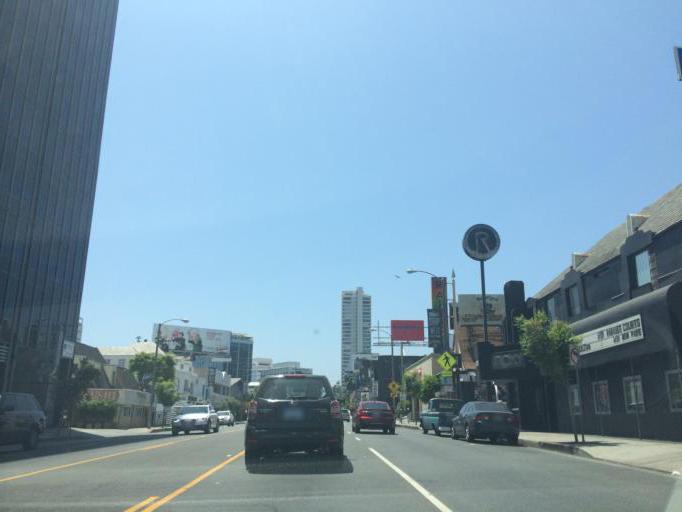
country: US
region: California
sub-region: Los Angeles County
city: Beverly Hills
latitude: 34.0907
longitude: -118.3877
